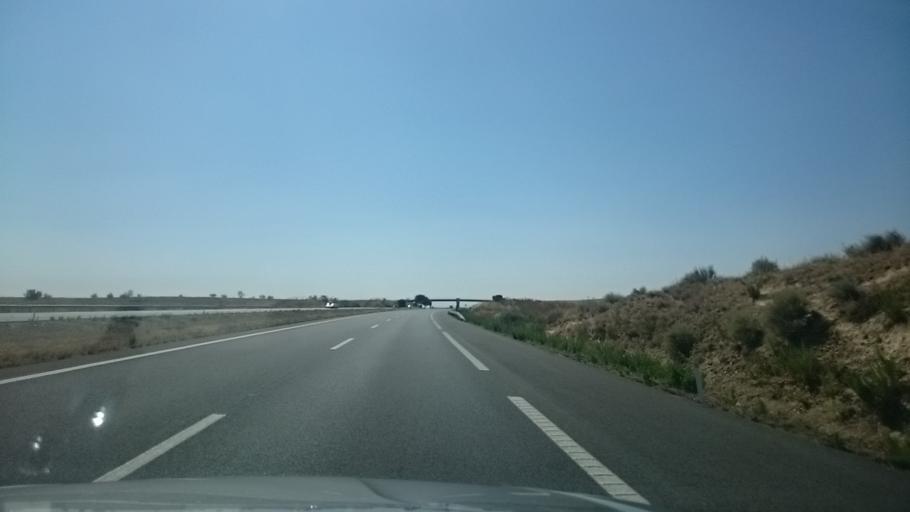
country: ES
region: Aragon
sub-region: Provincia de Zaragoza
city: Luceni
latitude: 41.8123
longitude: -1.2706
